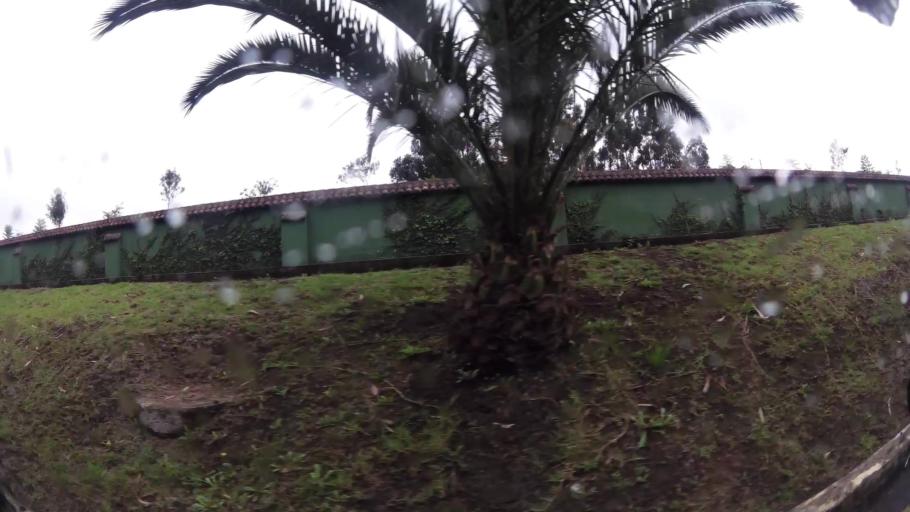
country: EC
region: Pichincha
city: Sangolqui
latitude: -0.3230
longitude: -78.4484
